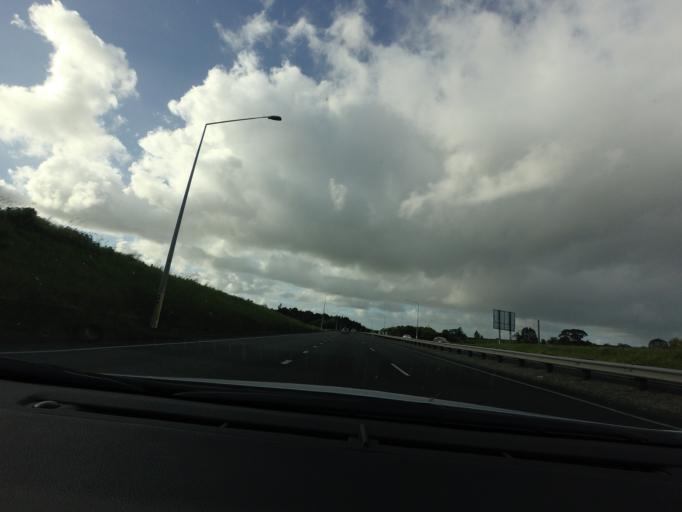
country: NZ
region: Auckland
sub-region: Auckland
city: Pukekohe East
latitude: -37.1892
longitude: 174.9815
